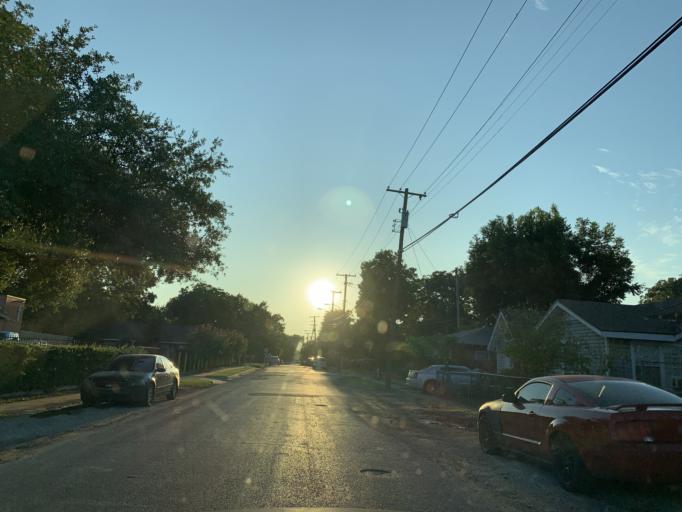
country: US
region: Texas
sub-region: Dallas County
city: Dallas
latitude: 32.7384
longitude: -96.8277
